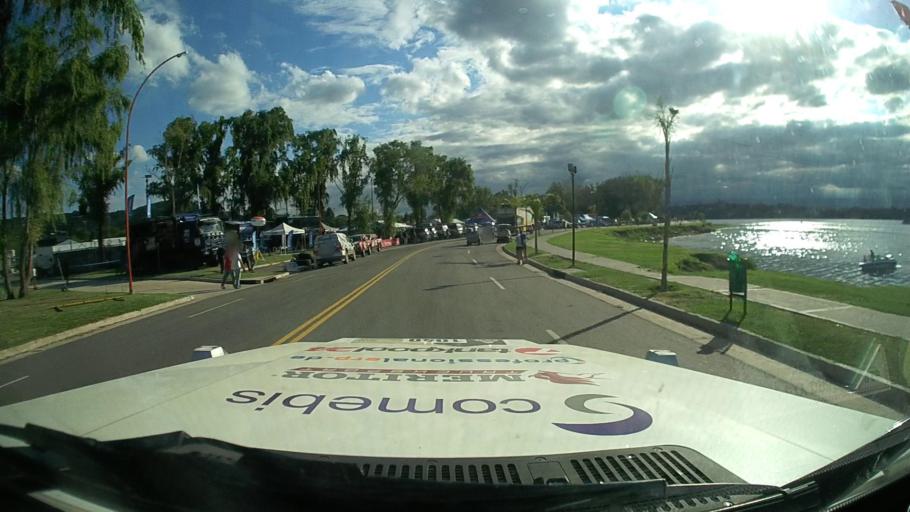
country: AR
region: Cordoba
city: Villa Carlos Paz
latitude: -31.3978
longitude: -64.4794
